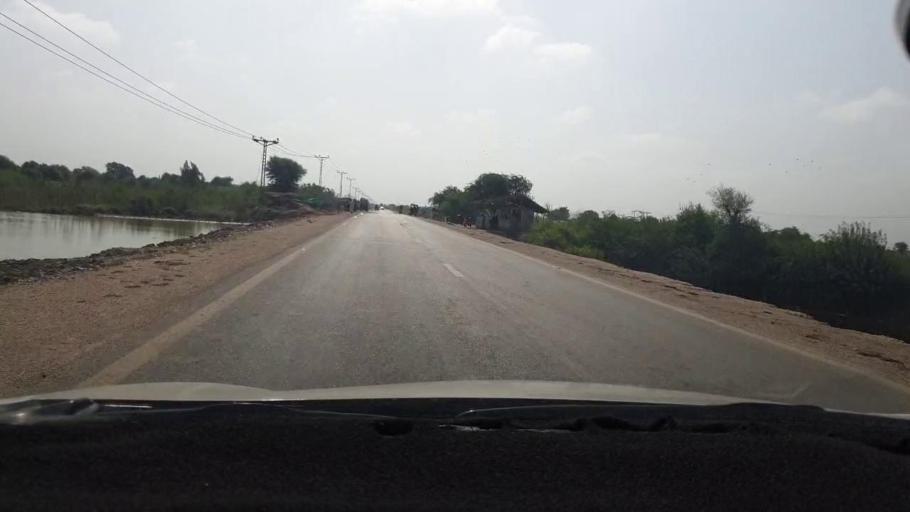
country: PK
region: Sindh
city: Mirpur Khas
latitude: 25.7651
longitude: 69.0734
